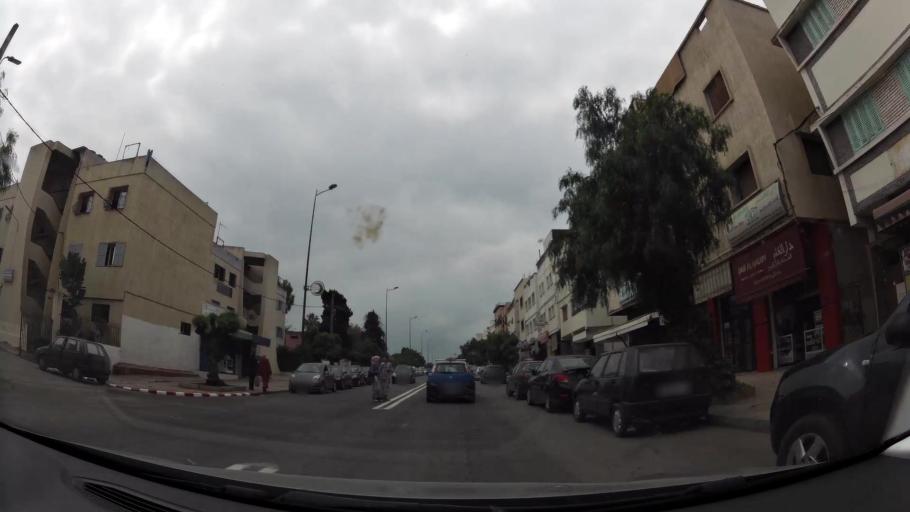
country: MA
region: Rabat-Sale-Zemmour-Zaer
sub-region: Rabat
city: Rabat
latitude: 33.9945
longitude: -6.8669
